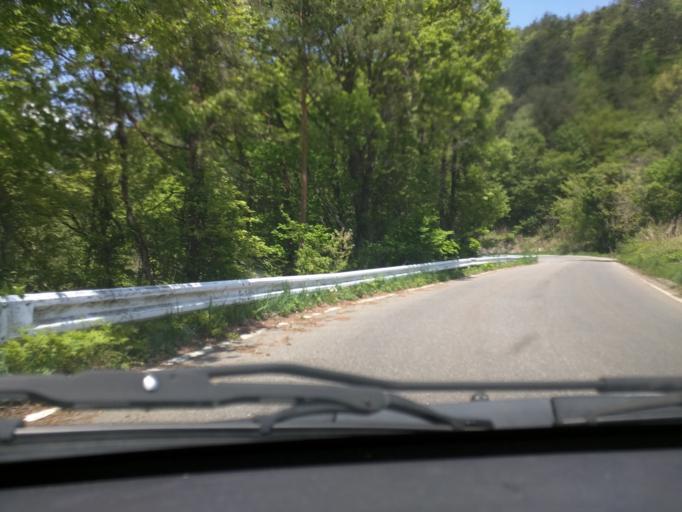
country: JP
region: Fukushima
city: Kitakata
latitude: 37.6387
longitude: 139.8091
